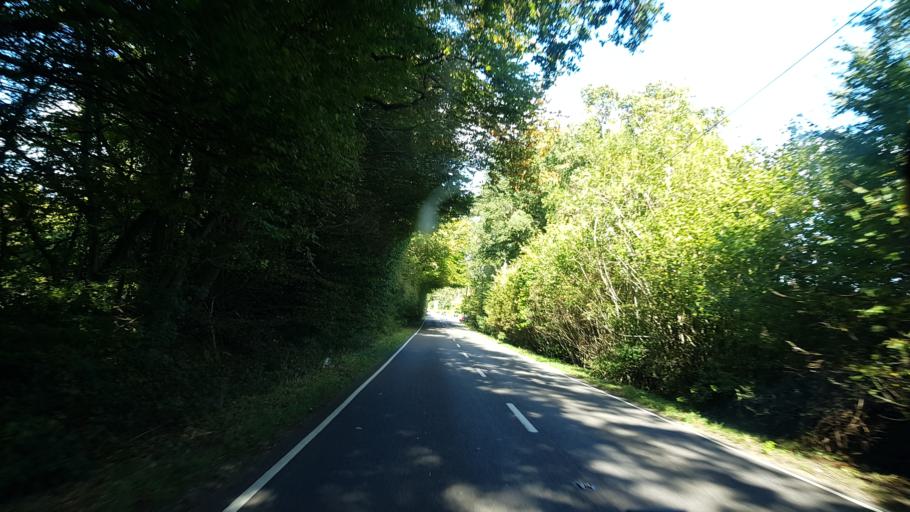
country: GB
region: England
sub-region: Surrey
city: Chiddingfold
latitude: 51.0860
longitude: -0.6477
